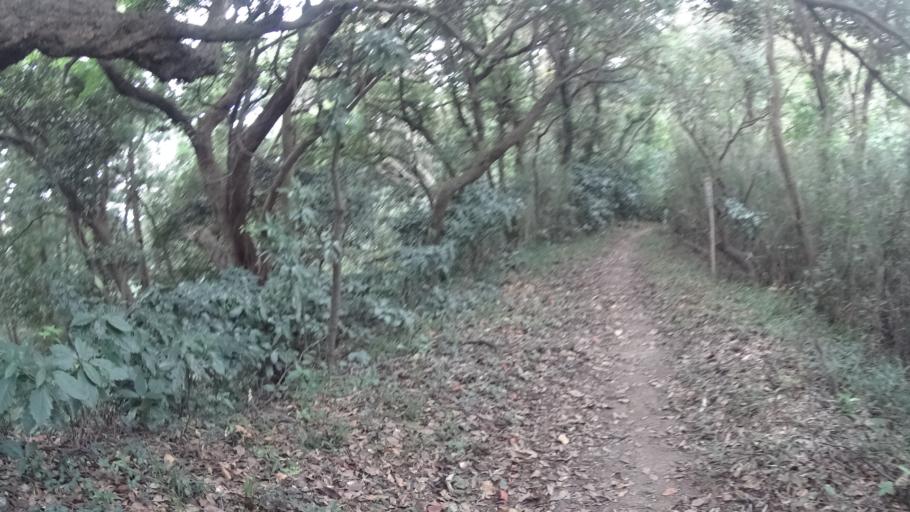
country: JP
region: Kanagawa
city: Zushi
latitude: 35.2893
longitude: 139.6107
